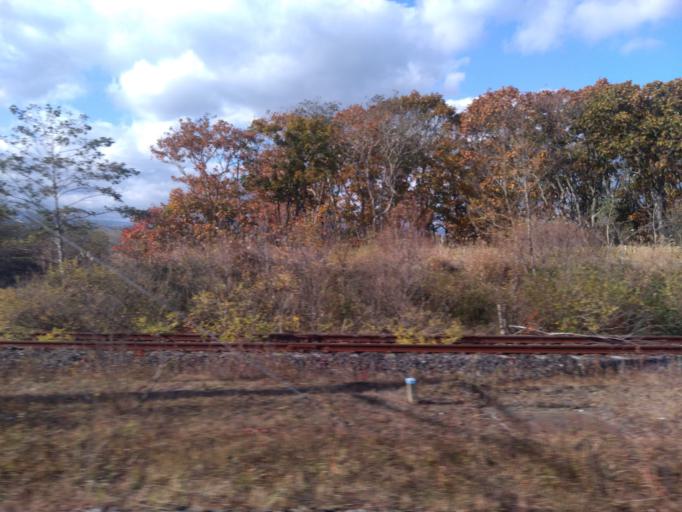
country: JP
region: Hokkaido
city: Shiraoi
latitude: 42.5171
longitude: 141.2990
